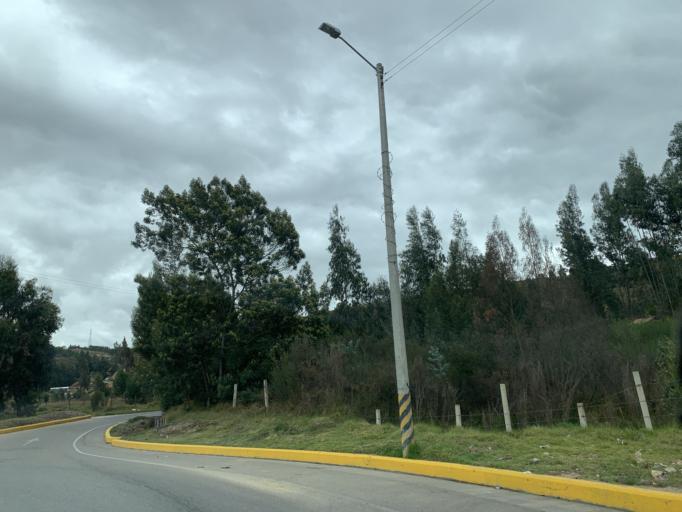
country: CO
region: Boyaca
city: Tunja
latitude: 5.5305
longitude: -73.3425
